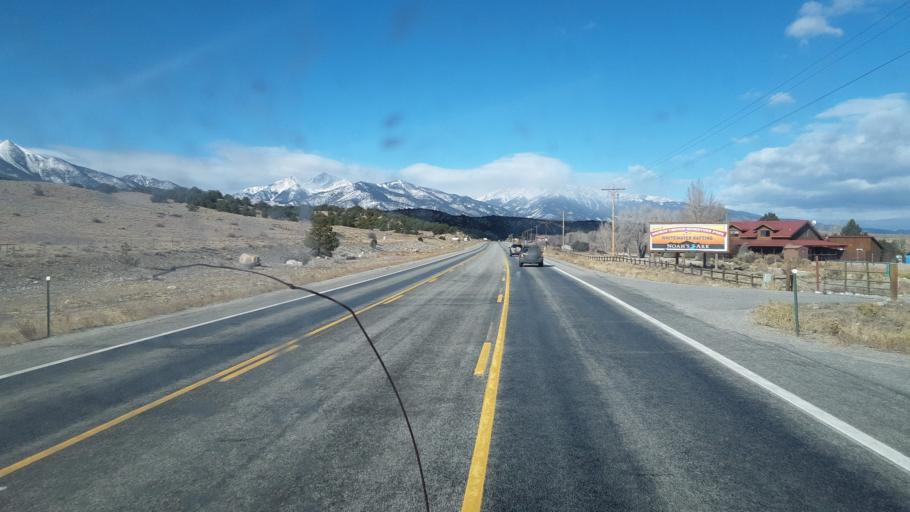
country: US
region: Colorado
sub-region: Chaffee County
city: Buena Vista
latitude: 38.7635
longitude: -106.0922
